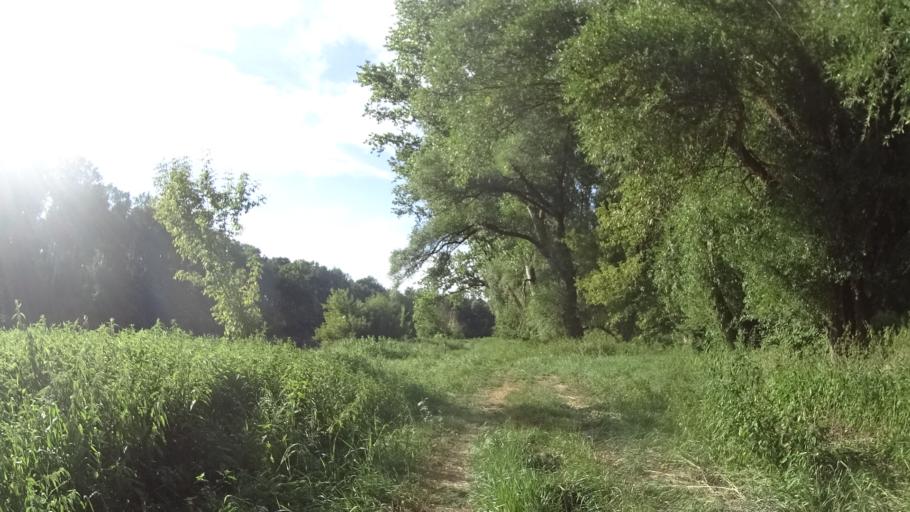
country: AT
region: Lower Austria
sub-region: Politischer Bezirk Mistelbach
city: Rabensburg
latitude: 48.6125
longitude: 16.9410
